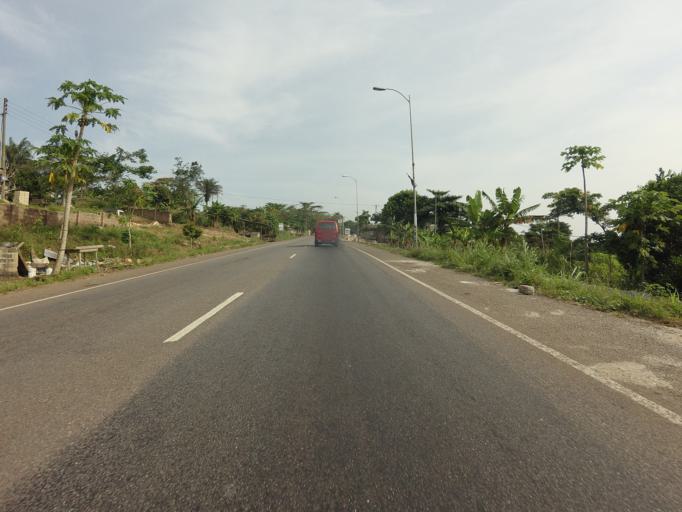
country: GH
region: Eastern
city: Aburi
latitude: 5.8294
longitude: -0.1845
